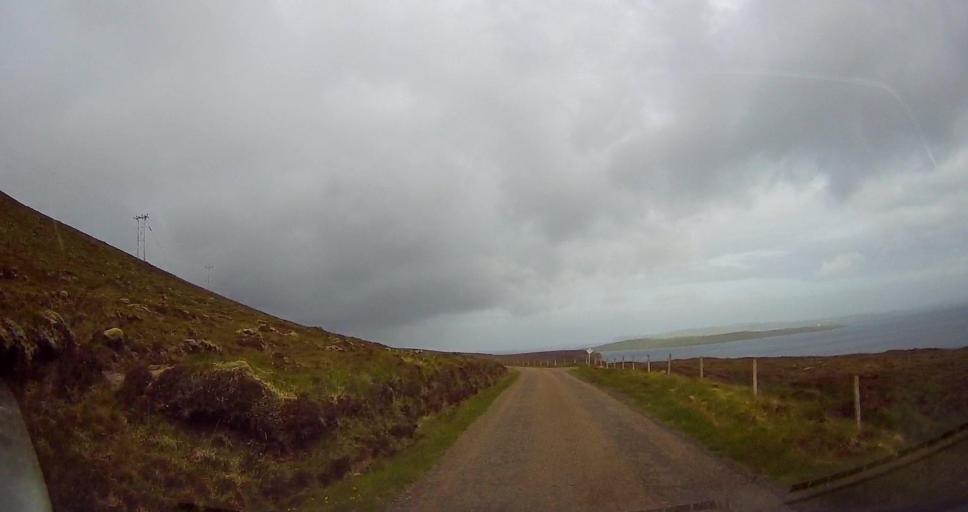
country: GB
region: Scotland
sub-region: Orkney Islands
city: Stromness
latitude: 58.8888
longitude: -3.2547
